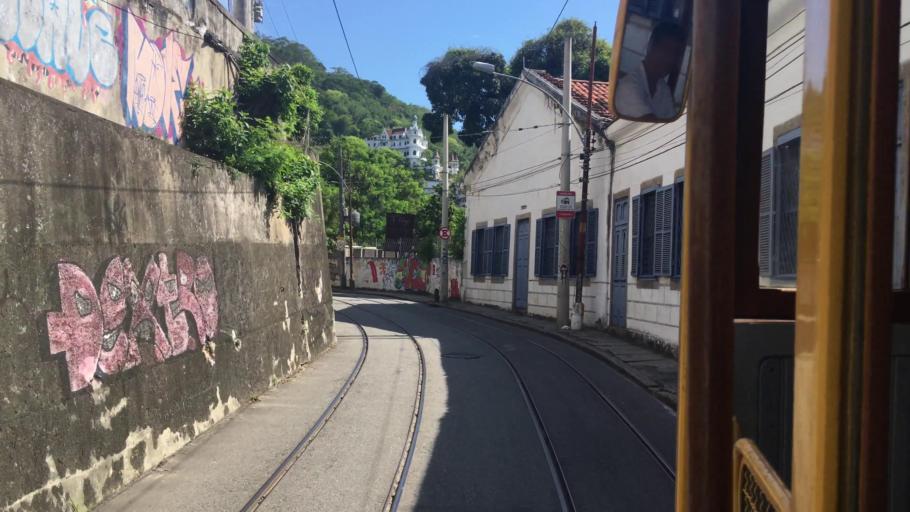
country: BR
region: Rio de Janeiro
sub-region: Rio De Janeiro
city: Rio de Janeiro
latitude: -22.9220
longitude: -43.1875
